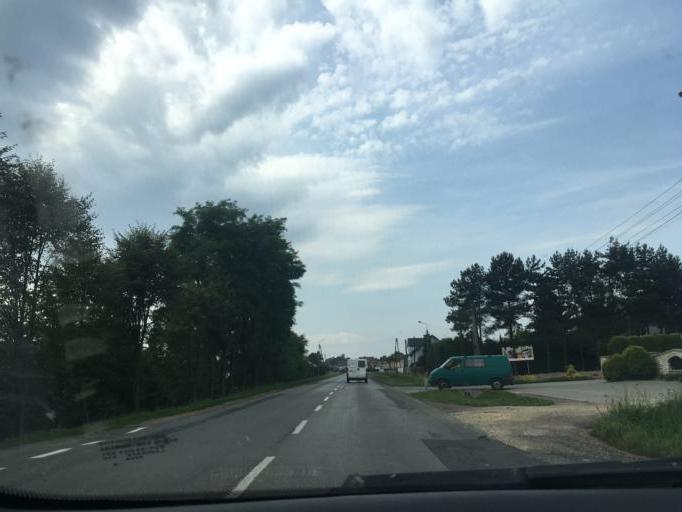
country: PL
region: Silesian Voivodeship
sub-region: Powiat raciborski
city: Kornowac
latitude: 50.0700
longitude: 18.3376
